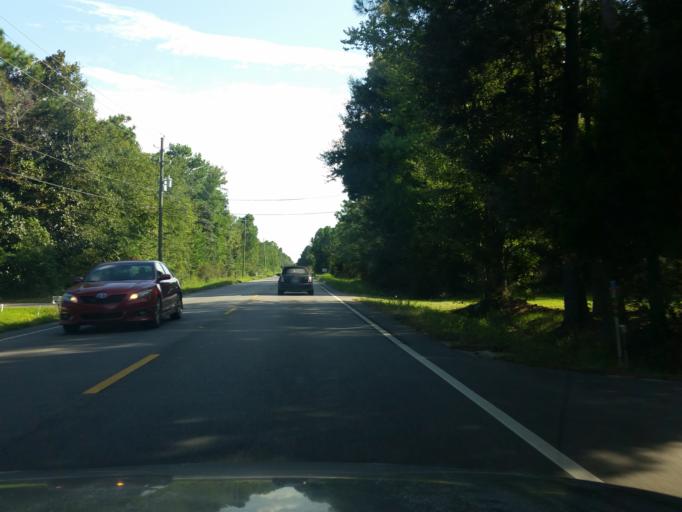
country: US
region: Alabama
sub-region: Mobile County
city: Theodore
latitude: 30.4898
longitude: -88.1121
